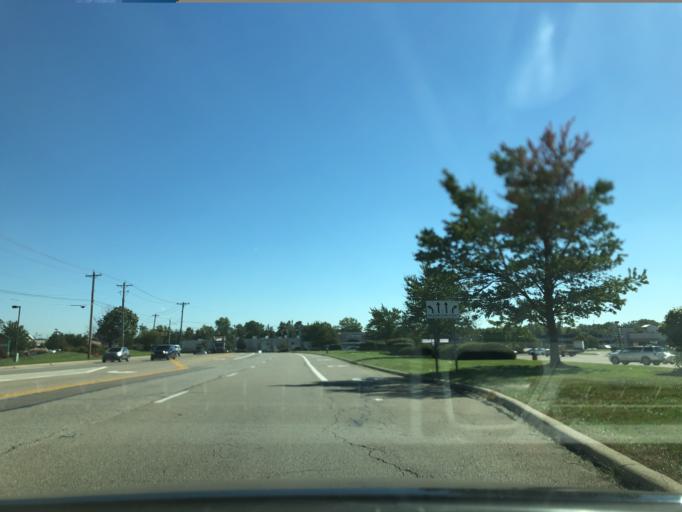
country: US
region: Ohio
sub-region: Hamilton County
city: Sixteen Mile Stand
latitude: 39.2919
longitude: -84.3069
